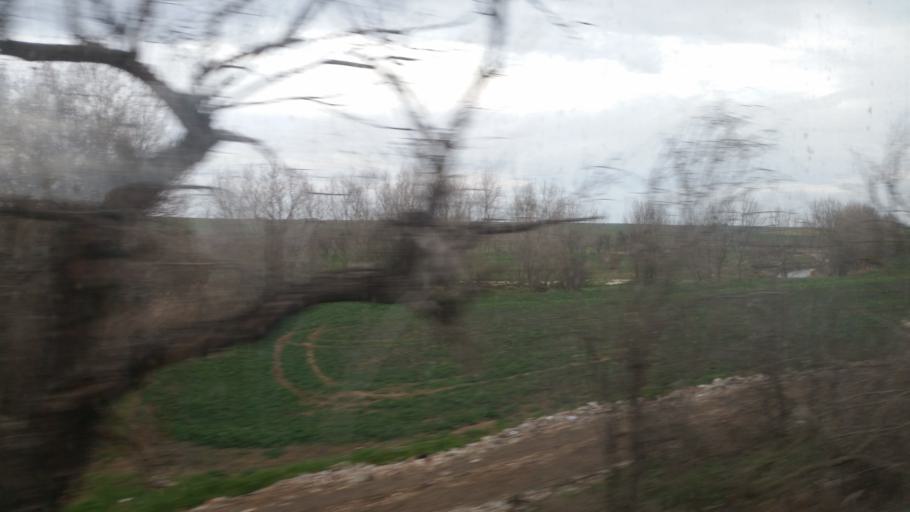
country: TR
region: Tekirdag
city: Marmaracik
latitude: 41.1455
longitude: 27.6554
